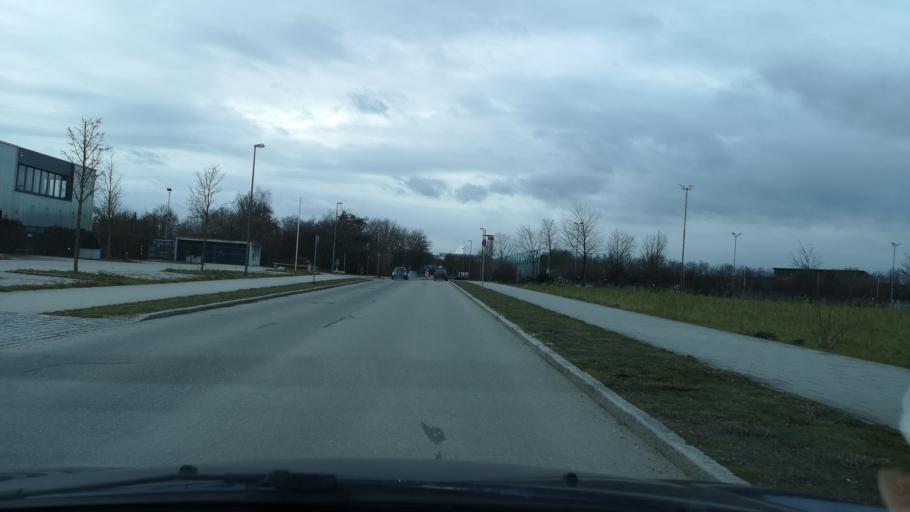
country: DE
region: Bavaria
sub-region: Upper Bavaria
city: Poing
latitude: 48.1743
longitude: 11.8156
